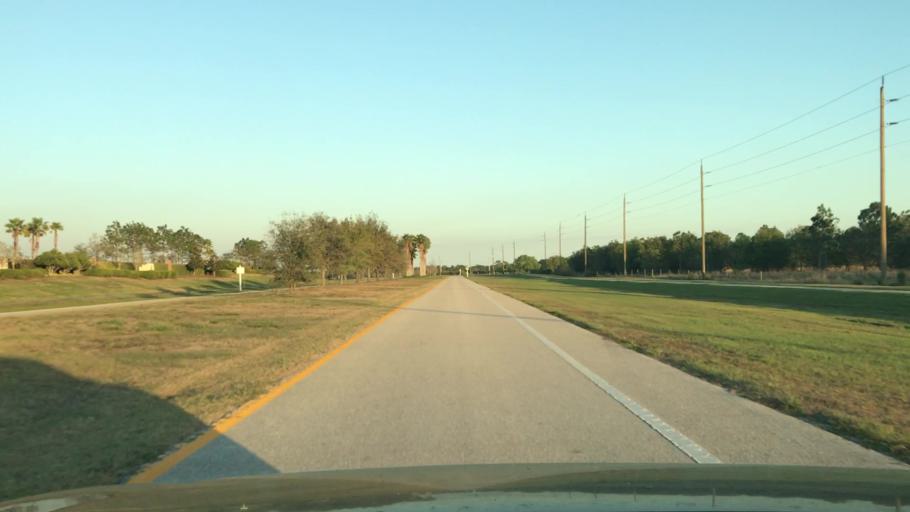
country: US
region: Florida
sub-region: Sarasota County
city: The Meadows
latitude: 27.3870
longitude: -82.3767
